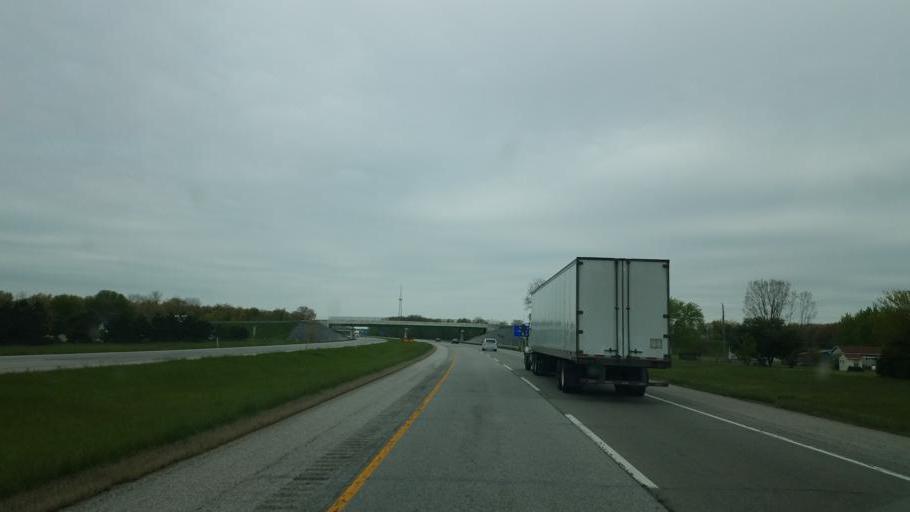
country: US
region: Michigan
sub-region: Saint Joseph County
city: White Pigeon
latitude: 41.7540
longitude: -85.6473
